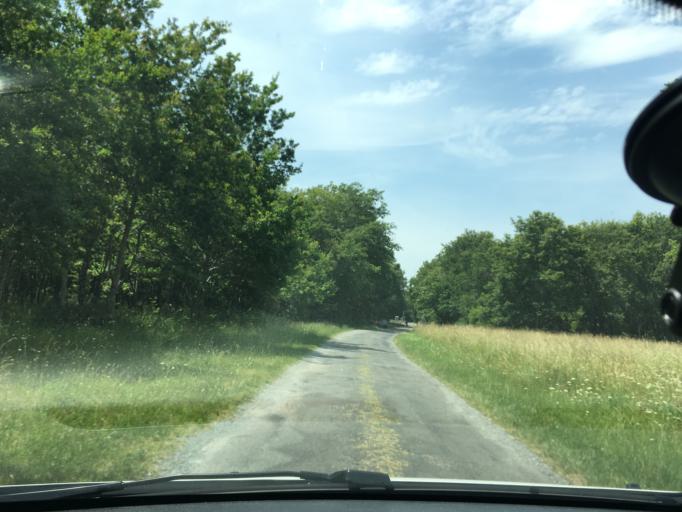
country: FR
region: Aquitaine
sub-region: Departement de la Gironde
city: Lesparre-Medoc
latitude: 45.2821
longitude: -0.9032
